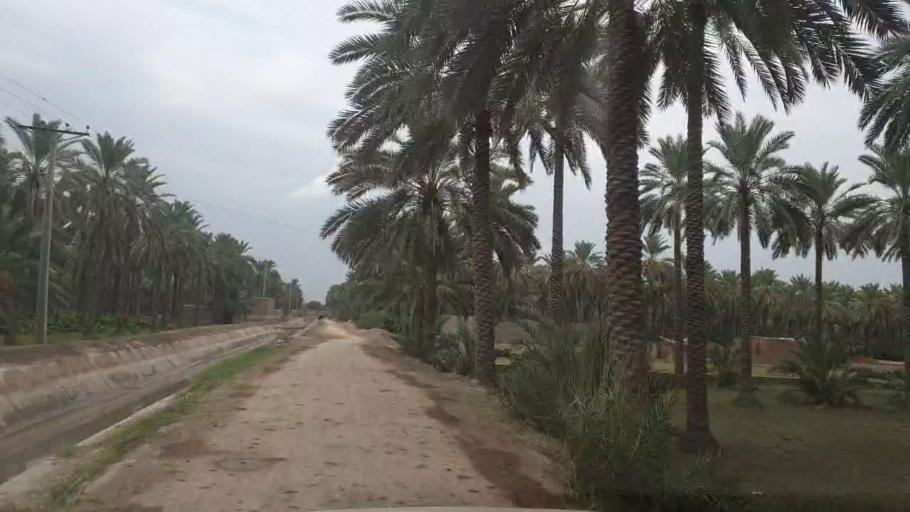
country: PK
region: Sindh
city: Khairpur
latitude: 27.6087
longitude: 68.8038
